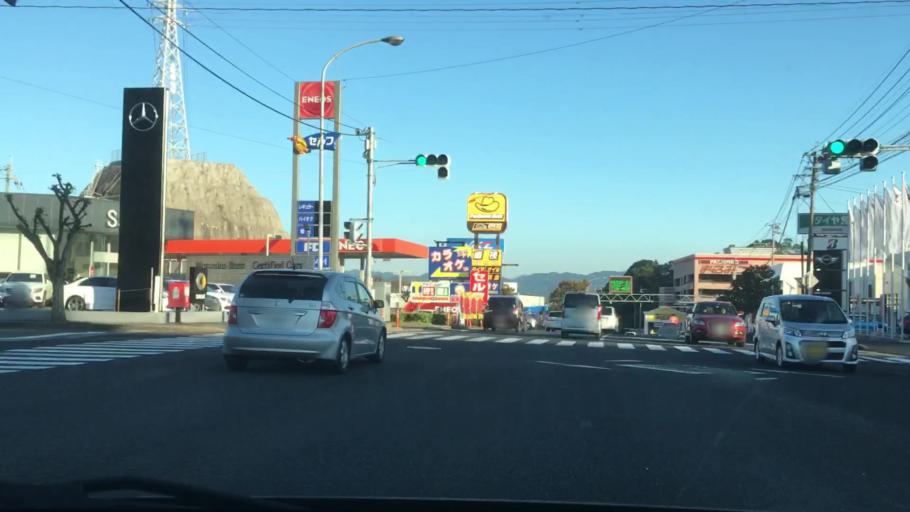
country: JP
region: Nagasaki
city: Sasebo
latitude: 33.1578
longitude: 129.7660
